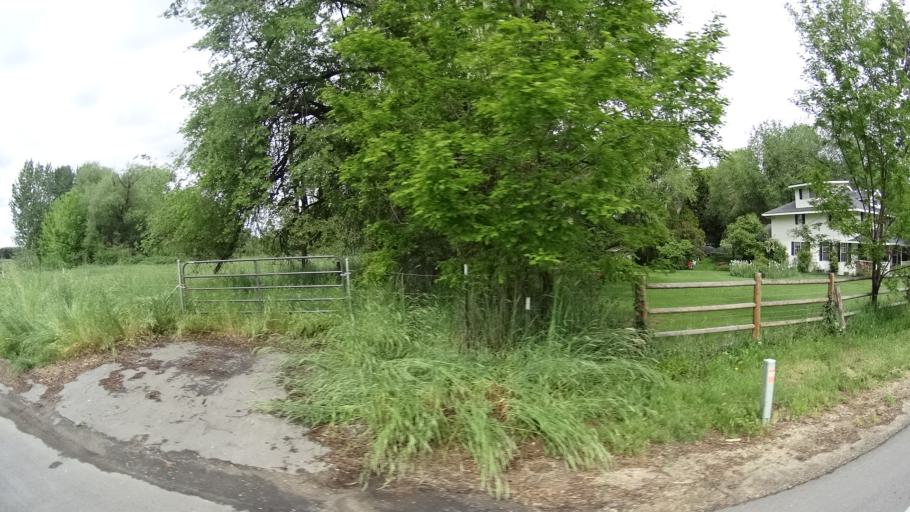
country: US
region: Idaho
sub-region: Ada County
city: Eagle
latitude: 43.7102
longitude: -116.3540
